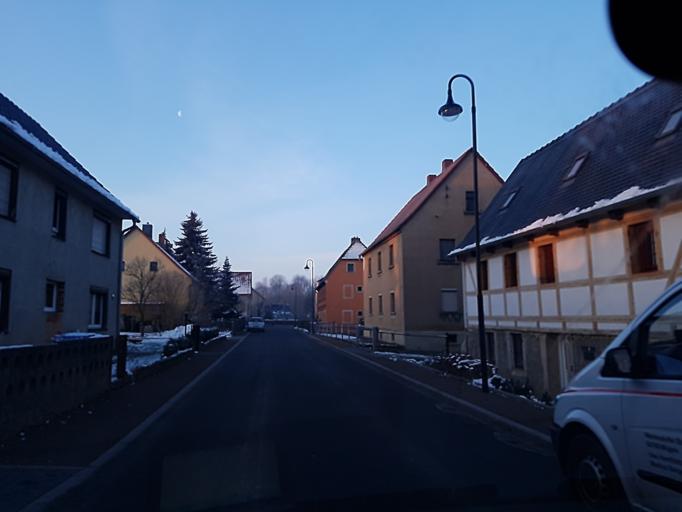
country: DE
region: Saxony
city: Naundorf
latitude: 51.2468
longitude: 13.0837
